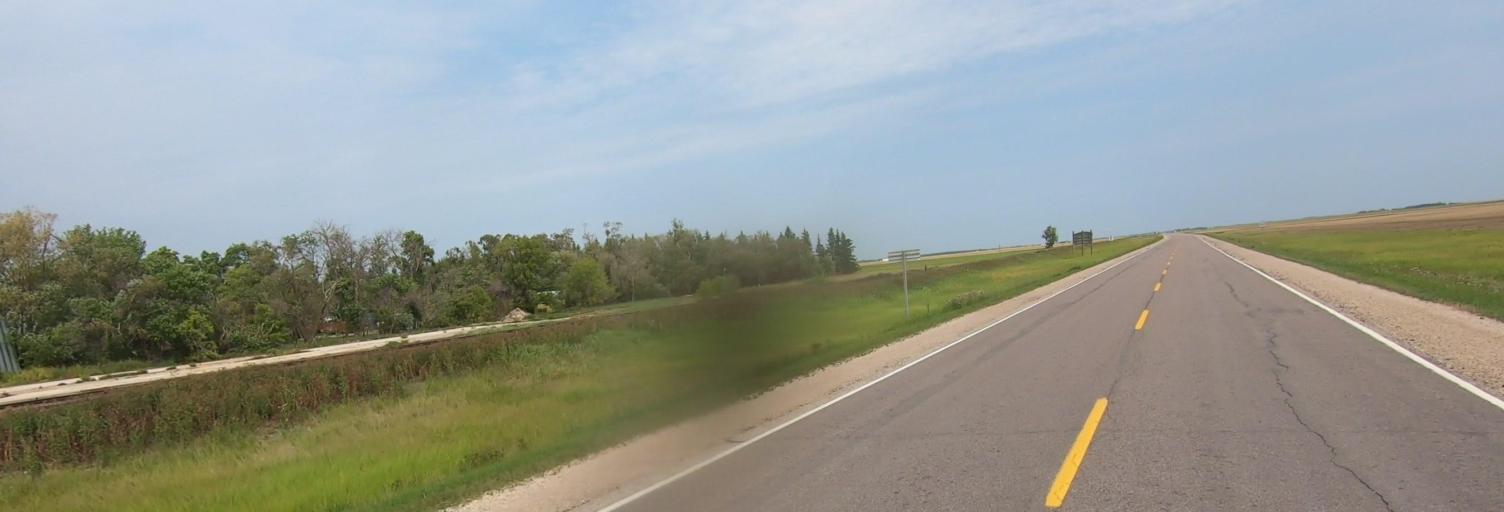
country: CA
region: Manitoba
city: Morris
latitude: 49.6161
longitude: -97.3203
